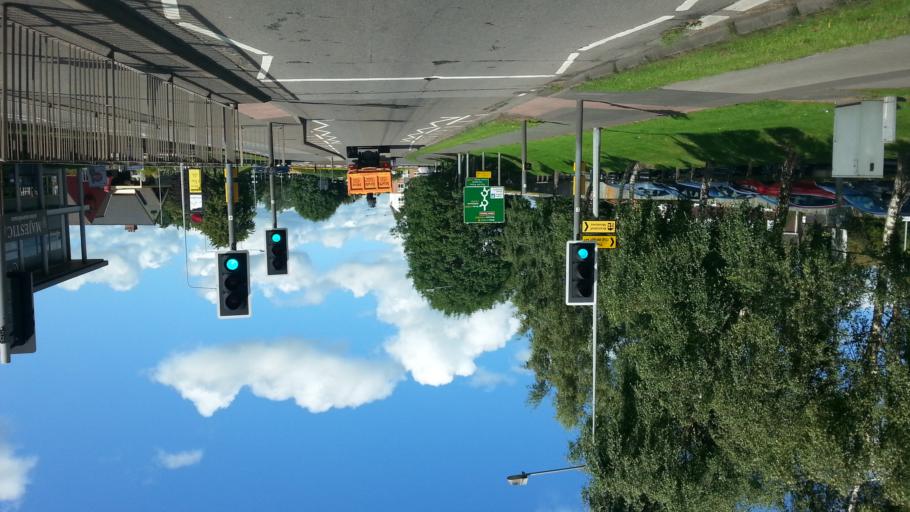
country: GB
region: England
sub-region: Staffordshire
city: Uttoxeter
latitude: 52.9001
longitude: -1.8604
